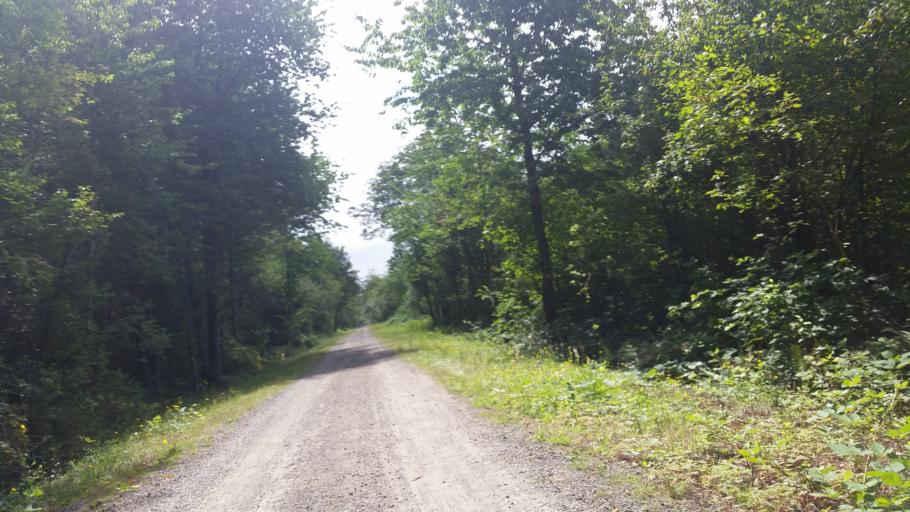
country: US
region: Washington
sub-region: King County
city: North Bend
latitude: 47.5084
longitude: -121.7911
